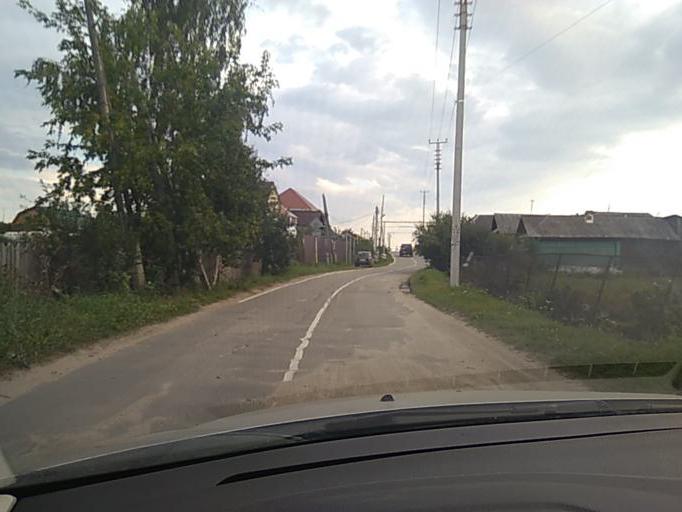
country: RU
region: Chelyabinsk
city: Kyshtym
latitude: 55.6971
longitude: 60.5324
